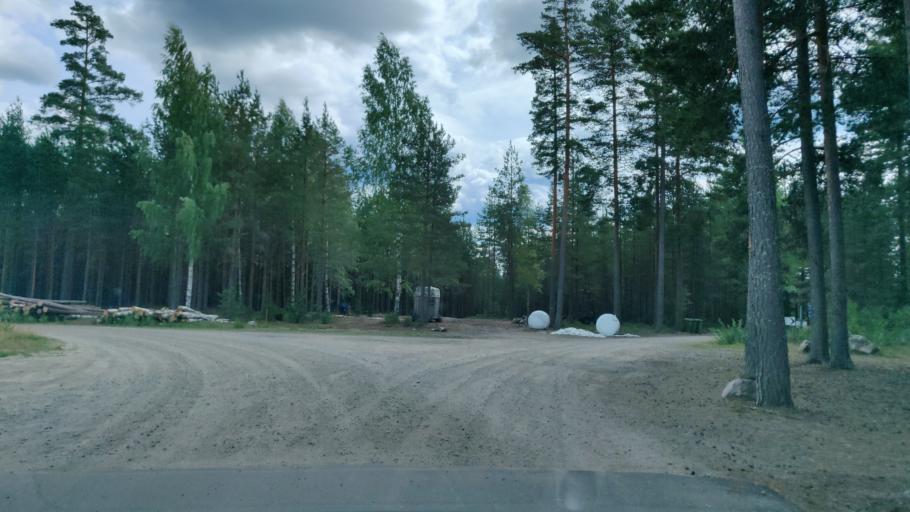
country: SE
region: Vaermland
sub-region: Hagfors Kommun
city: Hagfors
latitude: 60.0104
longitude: 13.6704
